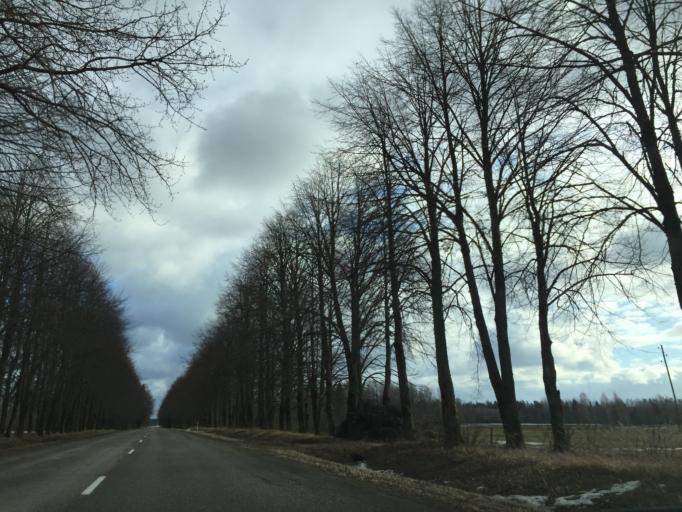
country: LV
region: Aloja
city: Staicele
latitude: 57.8805
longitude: 24.6623
